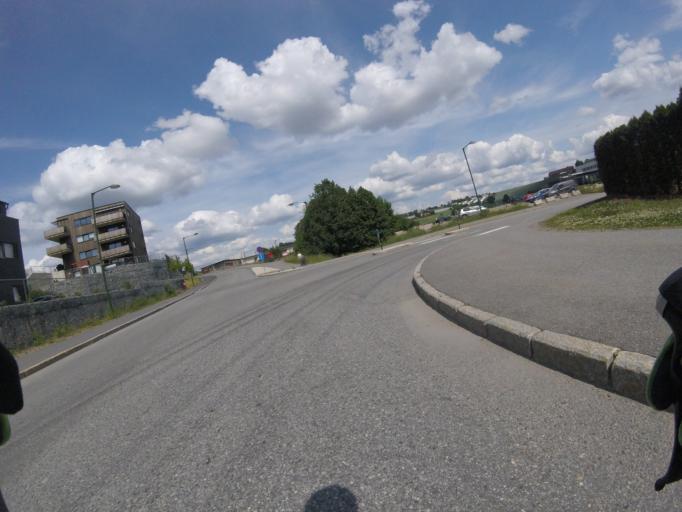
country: NO
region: Akershus
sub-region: Skedsmo
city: Lillestrom
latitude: 59.9762
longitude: 11.0413
